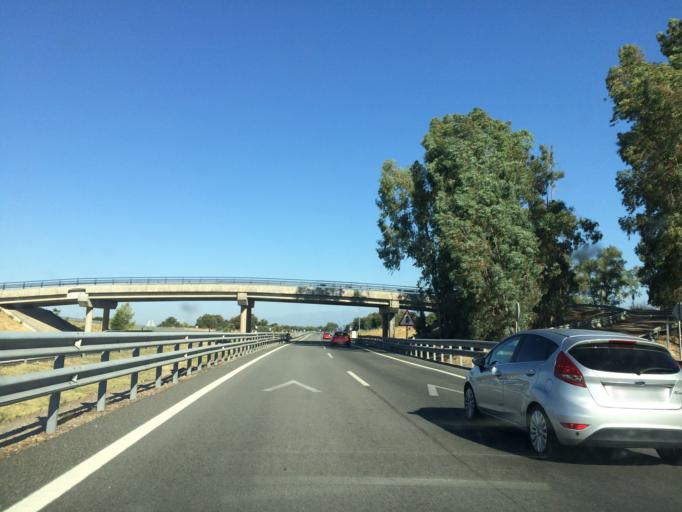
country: ES
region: Castille-La Mancha
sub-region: Province of Toledo
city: Alcanizo
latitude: 39.9188
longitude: -5.0808
